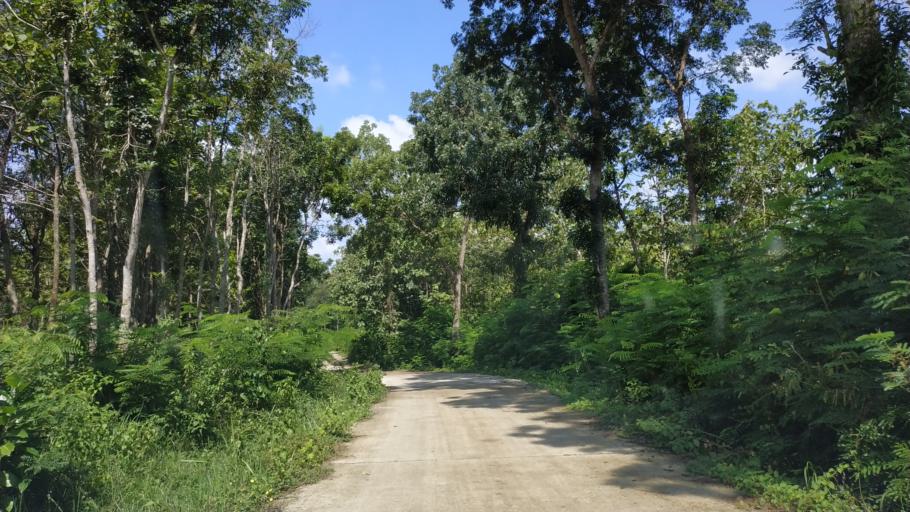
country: ID
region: Central Java
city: Guyangan
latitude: -7.0016
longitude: 111.0870
